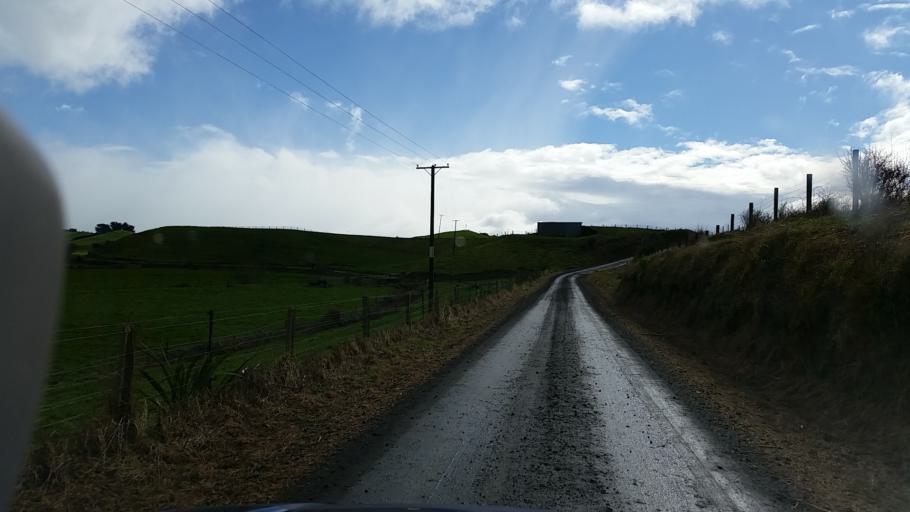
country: NZ
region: Taranaki
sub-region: South Taranaki District
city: Eltham
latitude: -39.2828
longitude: 174.3084
